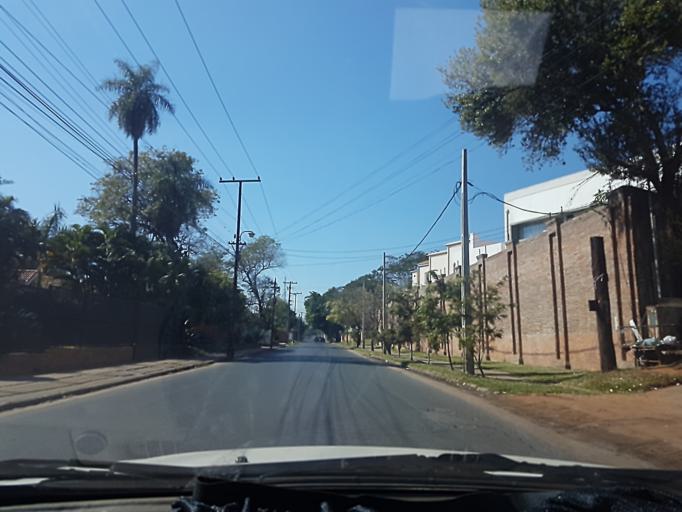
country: PY
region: Asuncion
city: Asuncion
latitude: -25.2589
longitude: -57.5724
